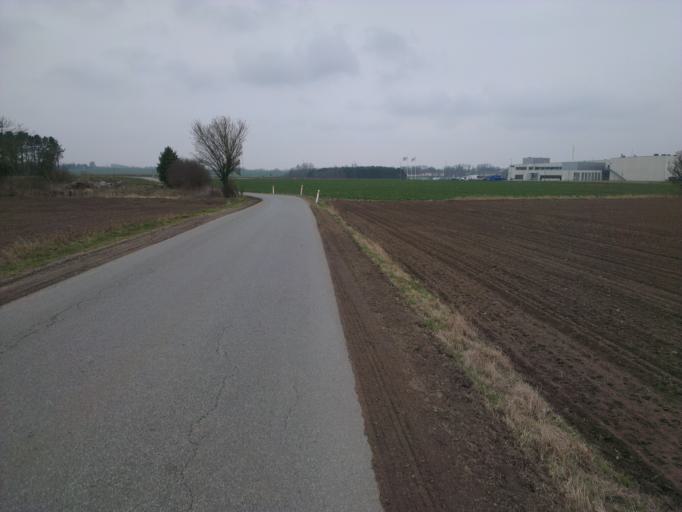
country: DK
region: Capital Region
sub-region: Frederikssund Kommune
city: Frederikssund
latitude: 55.8246
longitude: 12.1110
